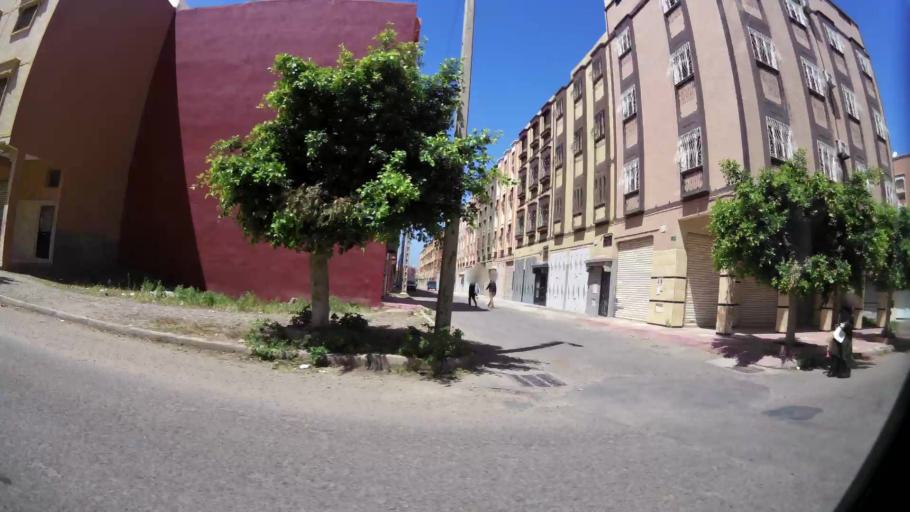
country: MA
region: Souss-Massa-Draa
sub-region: Inezgane-Ait Mellou
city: Inezgane
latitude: 30.3346
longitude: -9.5019
